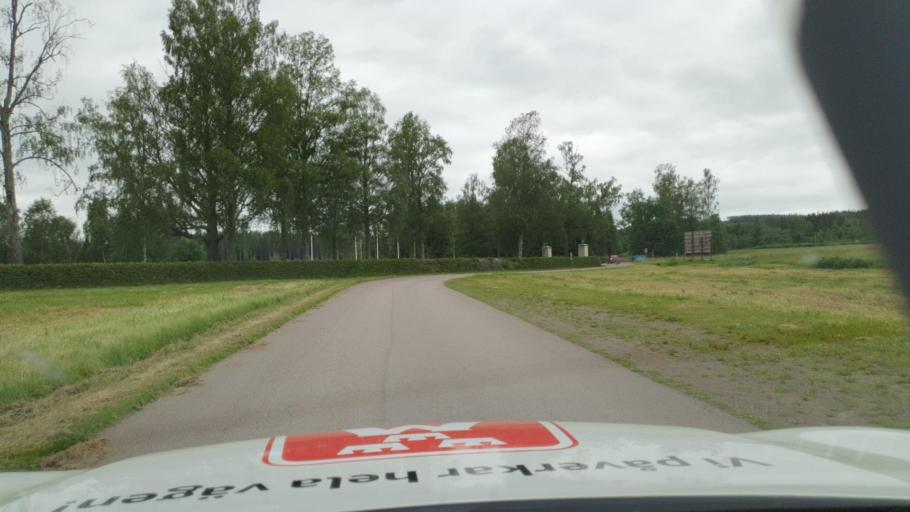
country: SE
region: Vaermland
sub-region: Sunne Kommun
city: Sunne
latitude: 59.8023
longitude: 13.1248
